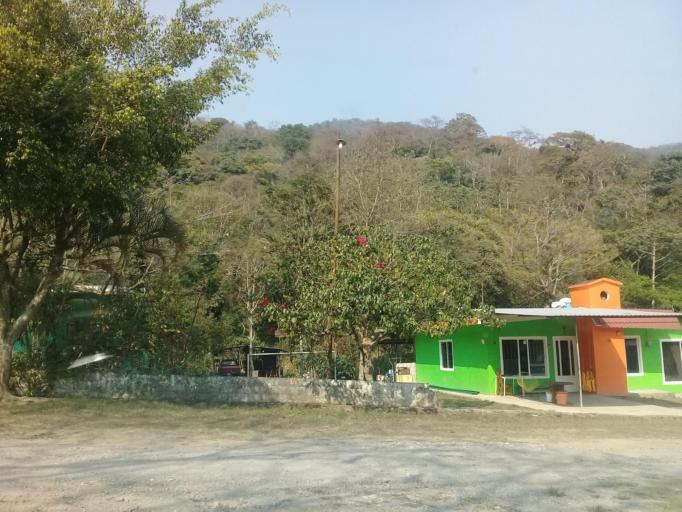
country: MX
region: Veracruz
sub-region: Ixtaczoquitlan
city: Campo Chico
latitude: 18.8389
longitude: -97.0290
